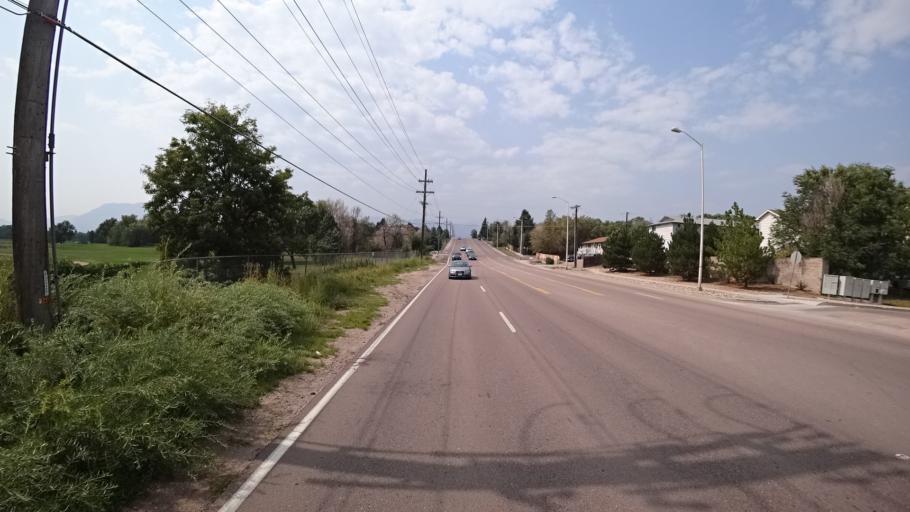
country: US
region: Colorado
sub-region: El Paso County
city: Stratmoor
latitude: 38.8253
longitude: -104.7615
